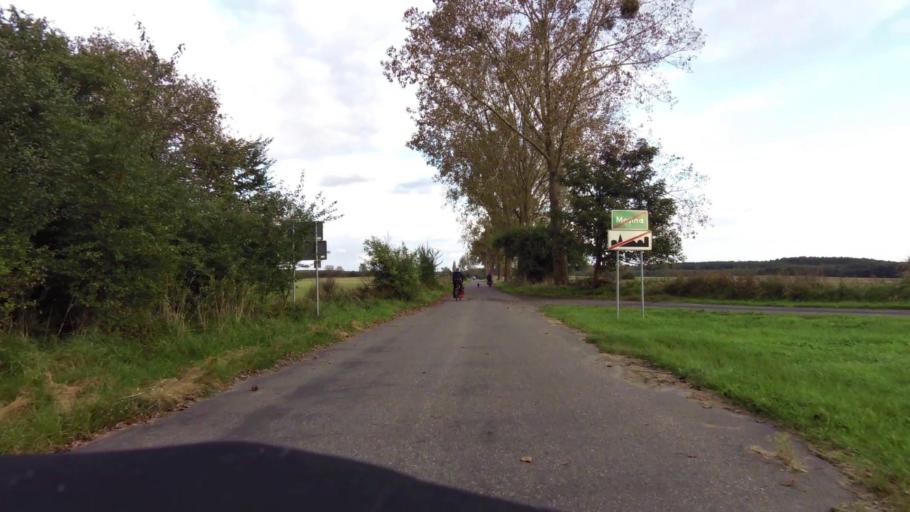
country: PL
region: West Pomeranian Voivodeship
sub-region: Powiat stargardzki
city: Dobrzany
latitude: 53.3856
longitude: 15.3615
